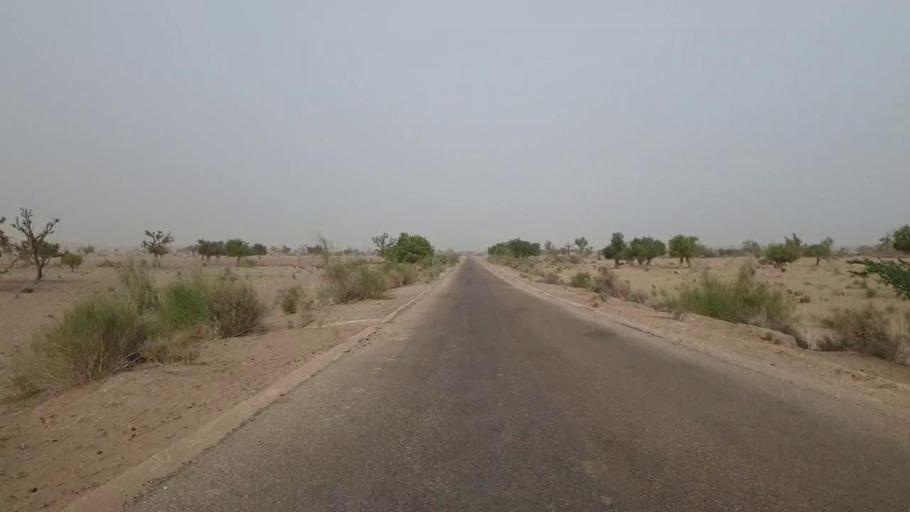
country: PK
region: Sindh
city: Islamkot
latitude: 24.5502
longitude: 70.3561
